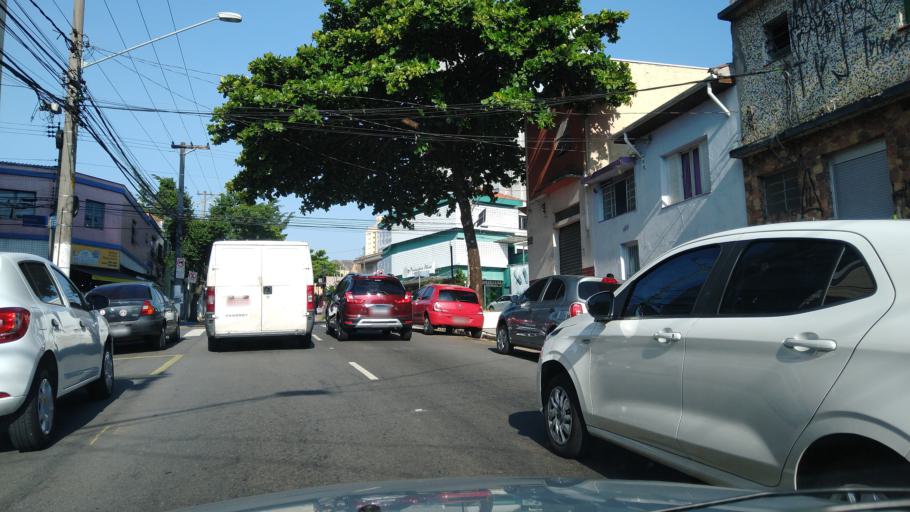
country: BR
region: Sao Paulo
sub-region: Sao Paulo
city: Sao Paulo
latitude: -23.5626
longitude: -46.5997
